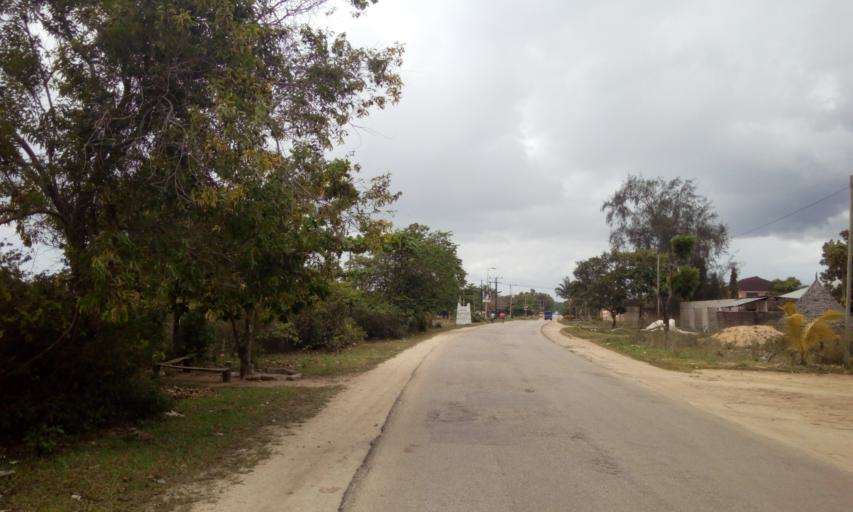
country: TZ
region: Zanzibar Central/South
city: Koani
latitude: -6.1996
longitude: 39.3103
